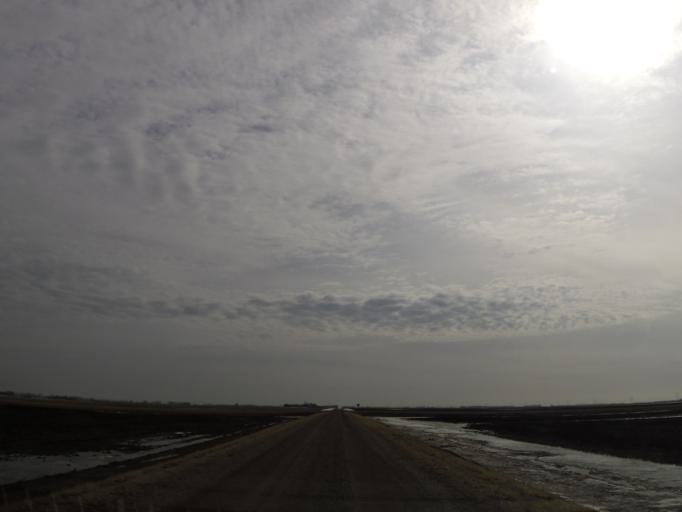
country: US
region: North Dakota
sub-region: Walsh County
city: Grafton
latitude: 48.4278
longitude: -97.2559
